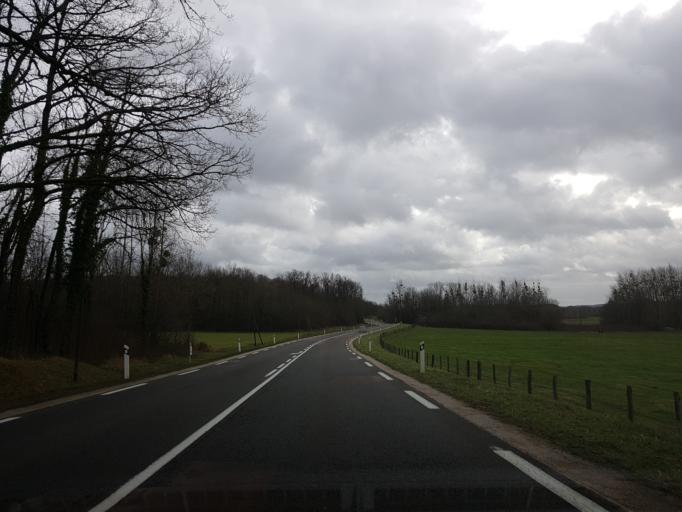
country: FR
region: Champagne-Ardenne
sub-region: Departement de la Haute-Marne
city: Chalindrey
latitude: 47.8233
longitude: 5.4811
